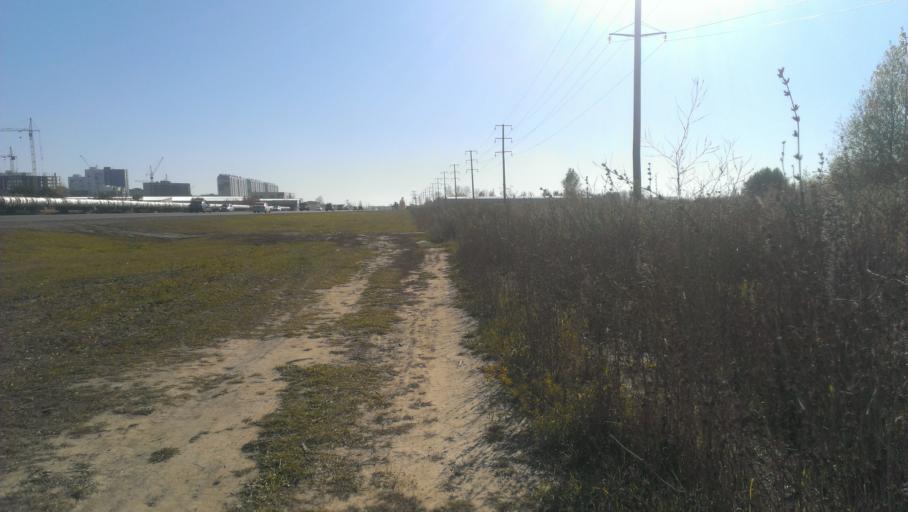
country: RU
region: Altai Krai
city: Novosilikatnyy
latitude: 53.3432
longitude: 83.6357
